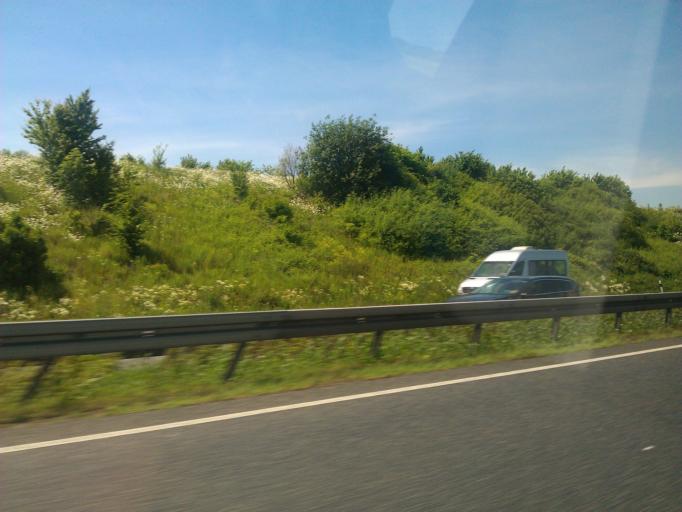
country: DE
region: North Rhine-Westphalia
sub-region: Regierungsbezirk Koln
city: Konigswinter
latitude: 50.7151
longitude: 7.2421
